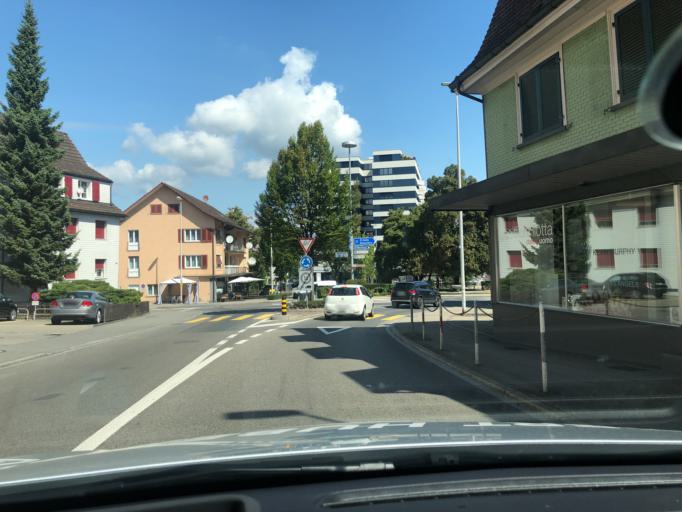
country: CH
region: Thurgau
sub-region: Kreuzlingen District
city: Kreuzlingen
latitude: 47.6442
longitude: 9.1709
